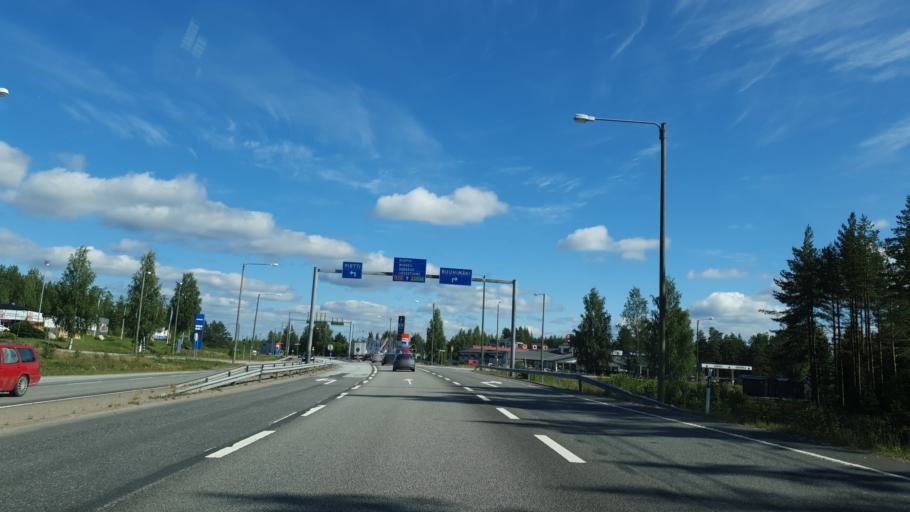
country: FI
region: Central Finland
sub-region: Jyvaeskylae
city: Toivakka
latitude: 62.2474
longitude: 26.1326
